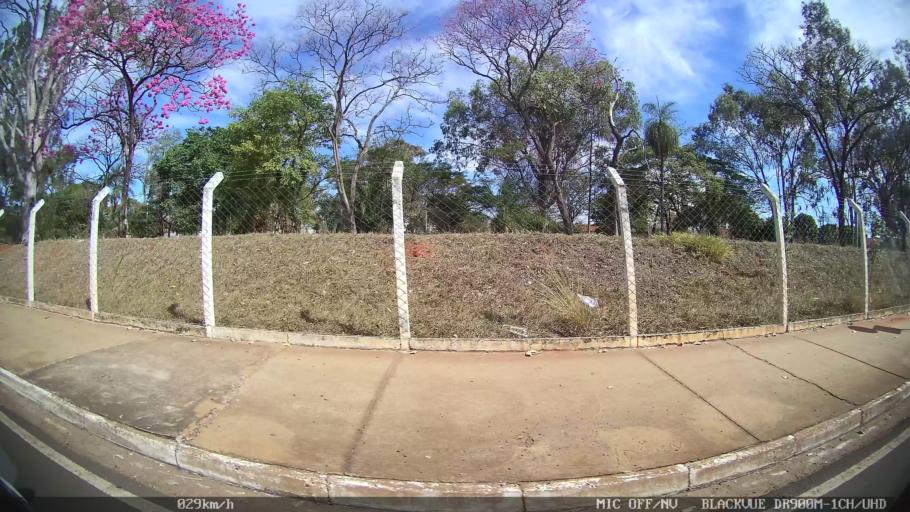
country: BR
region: Sao Paulo
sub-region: Sao Jose Do Rio Preto
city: Sao Jose do Rio Preto
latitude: -20.8194
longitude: -49.3567
